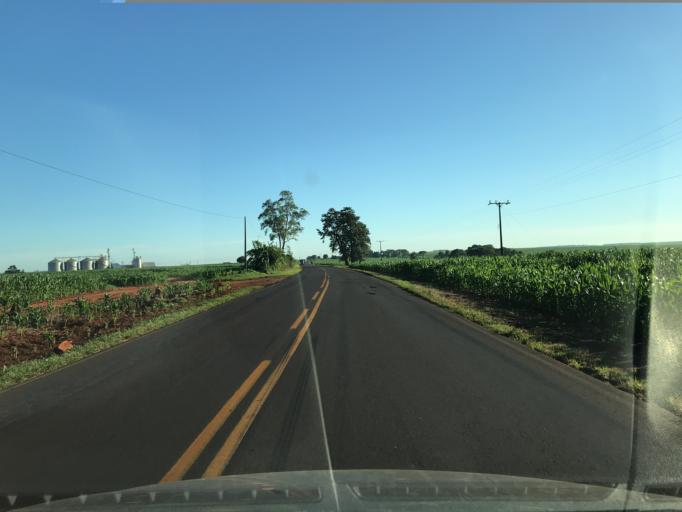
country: BR
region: Parana
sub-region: Palotina
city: Palotina
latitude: -24.1254
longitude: -53.8503
